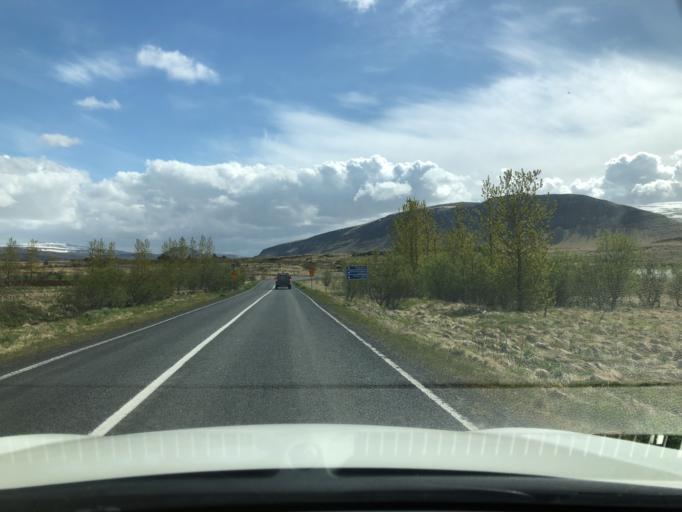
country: IS
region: Capital Region
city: Mosfellsbaer
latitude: 64.3436
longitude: -21.6113
